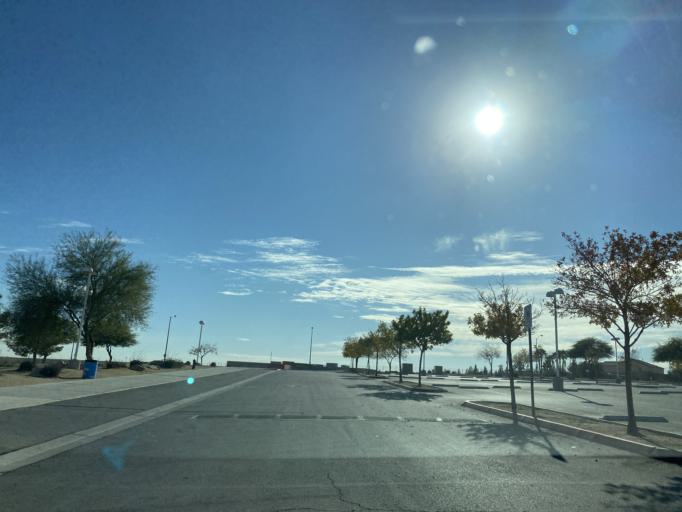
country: US
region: Nevada
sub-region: Clark County
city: North Las Vegas
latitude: 36.2848
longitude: -115.1432
